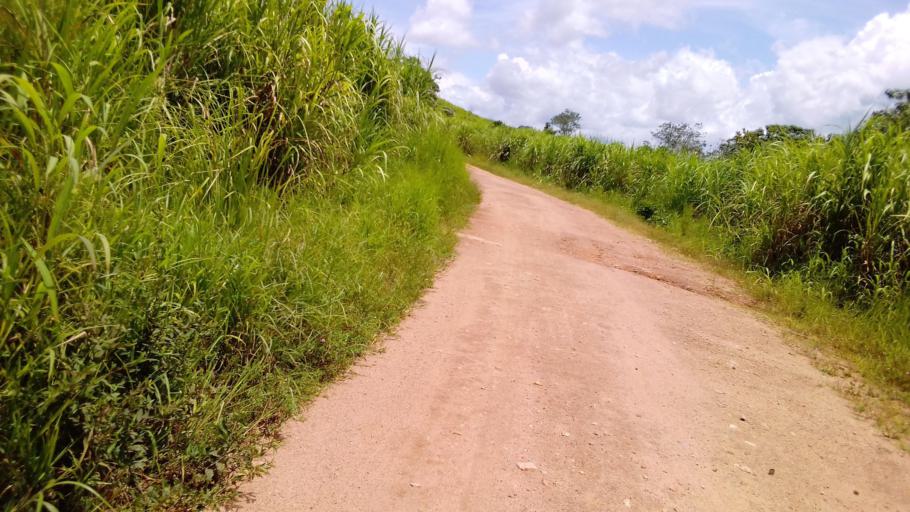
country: SL
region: Eastern Province
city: Koidu
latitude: 8.6714
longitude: -10.9414
